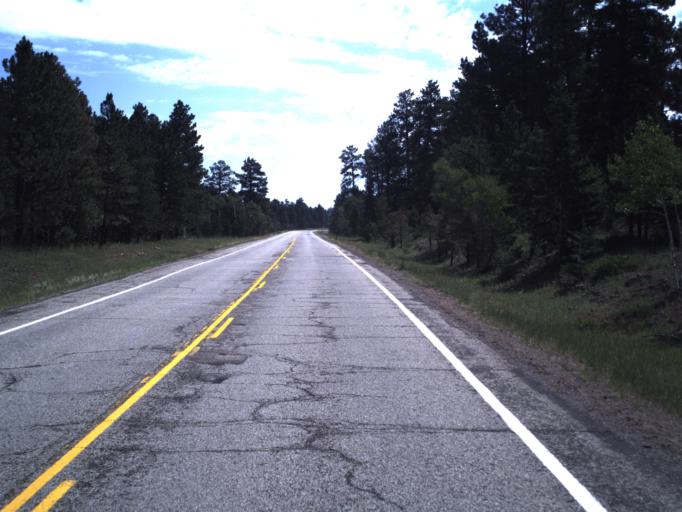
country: US
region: Utah
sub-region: Daggett County
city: Manila
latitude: 40.8519
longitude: -109.6114
